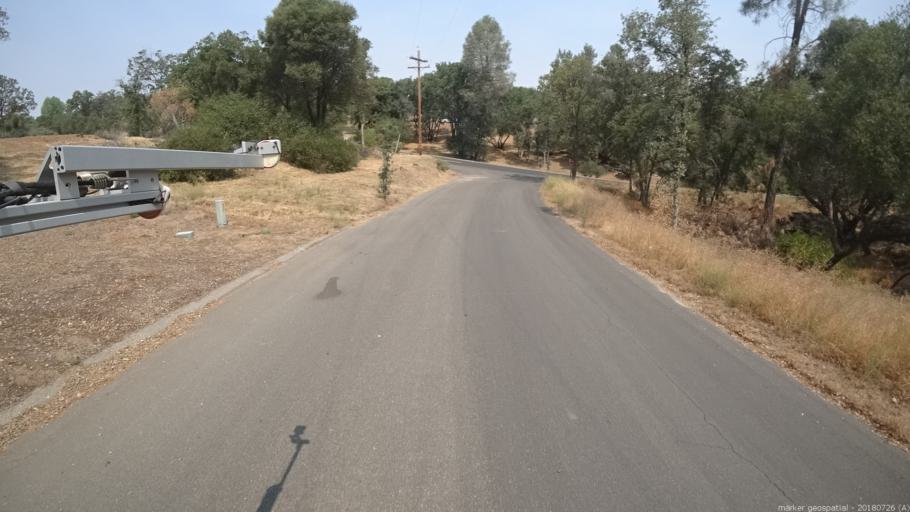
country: US
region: California
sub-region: Madera County
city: Coarsegold
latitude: 37.2503
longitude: -119.6896
